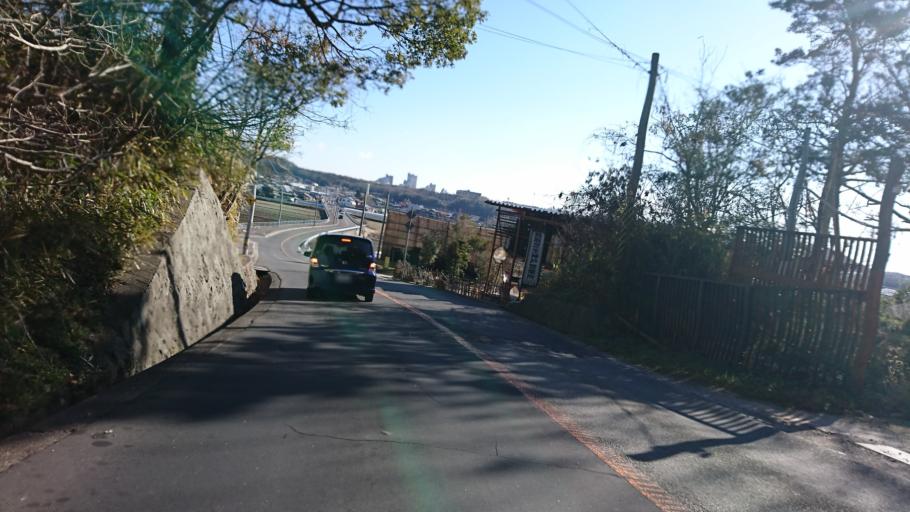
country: JP
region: Hyogo
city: Akashi
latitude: 34.7121
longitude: 134.9762
